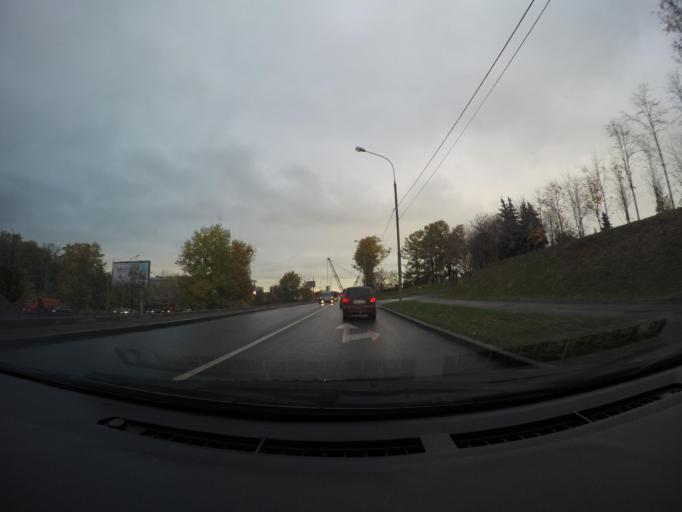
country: RU
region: Moskovskaya
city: Kastanayevo
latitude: 55.7301
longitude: 37.4928
